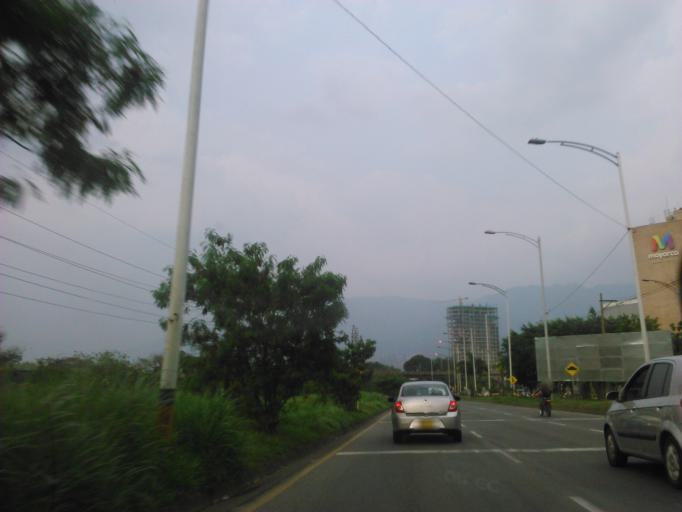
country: CO
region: Antioquia
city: Sabaneta
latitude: 6.1620
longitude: -75.6078
